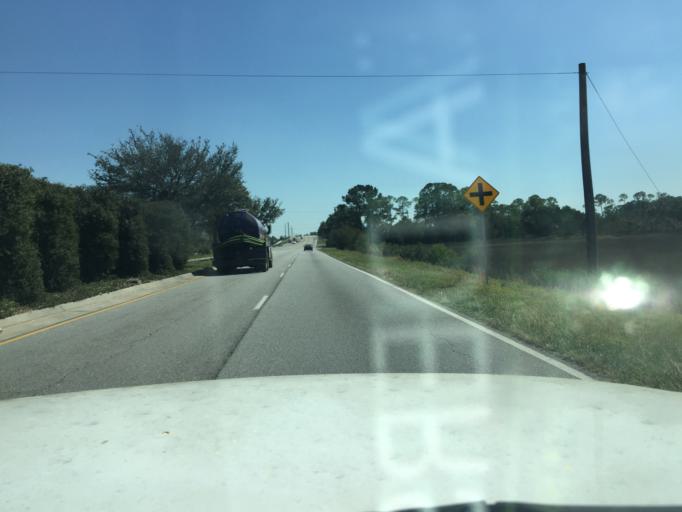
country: US
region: Georgia
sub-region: Chatham County
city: Whitemarsh Island
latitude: 32.0238
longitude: -80.9969
